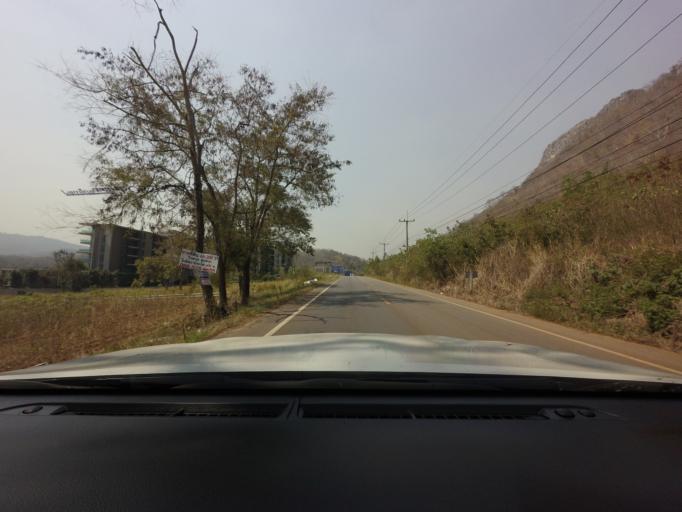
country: TH
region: Sara Buri
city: Muak Lek
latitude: 14.5553
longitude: 101.3119
